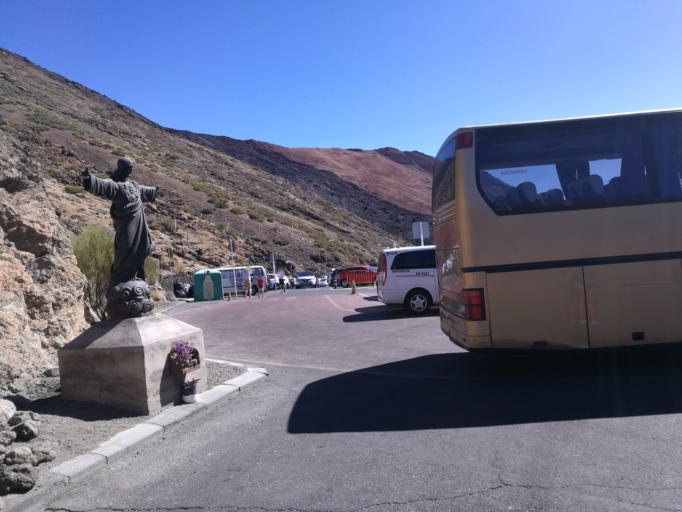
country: ES
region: Canary Islands
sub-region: Provincia de Santa Cruz de Tenerife
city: Vilaflor
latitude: 28.2548
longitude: -16.6260
